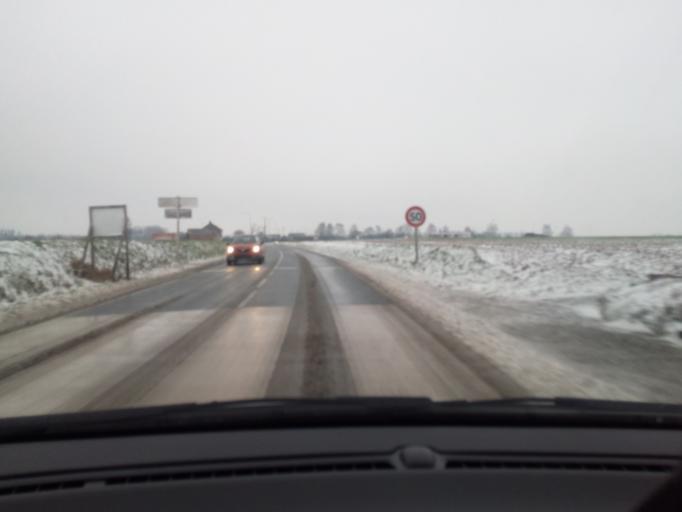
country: FR
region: Nord-Pas-de-Calais
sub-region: Departement du Nord
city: La Longueville
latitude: 50.3360
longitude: 3.8731
